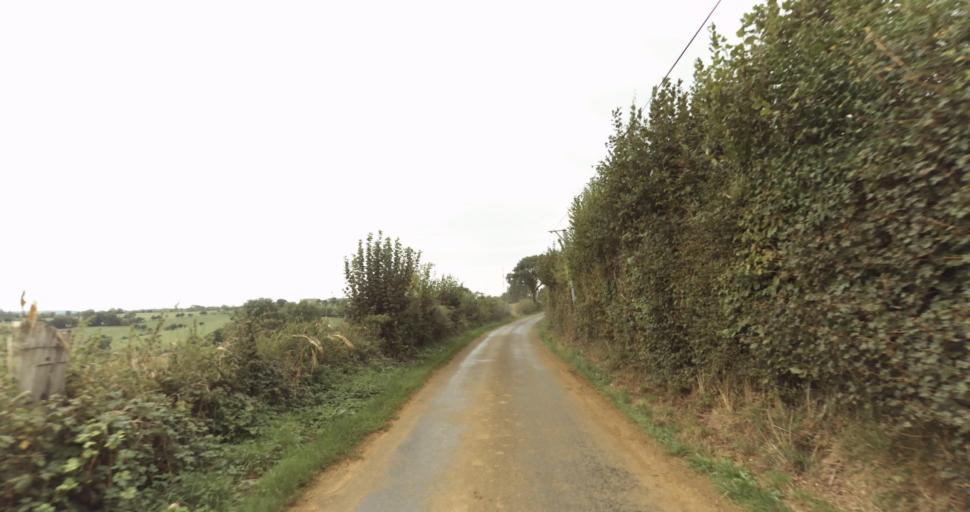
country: FR
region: Lower Normandy
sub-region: Departement de l'Orne
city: Gace
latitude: 48.7241
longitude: 0.3216
